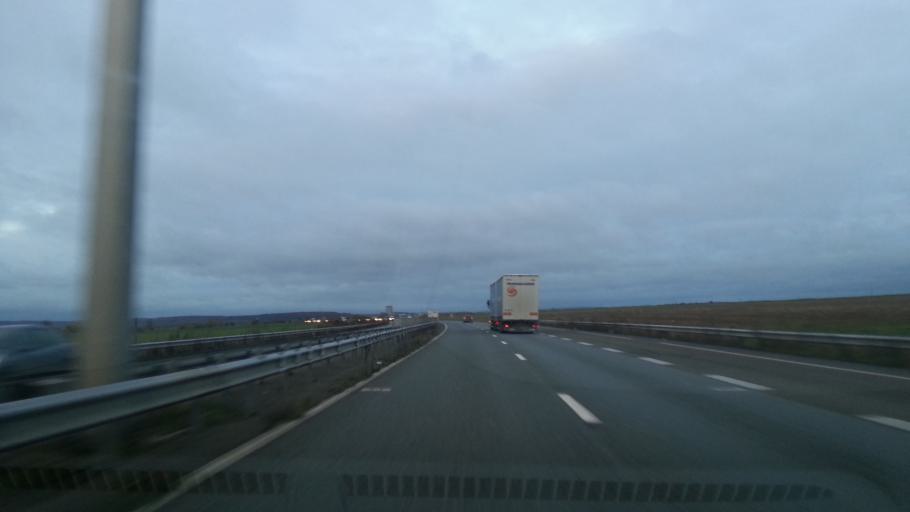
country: FR
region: Picardie
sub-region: Departement de l'Oise
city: Bresles
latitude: 49.4150
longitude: 2.2995
